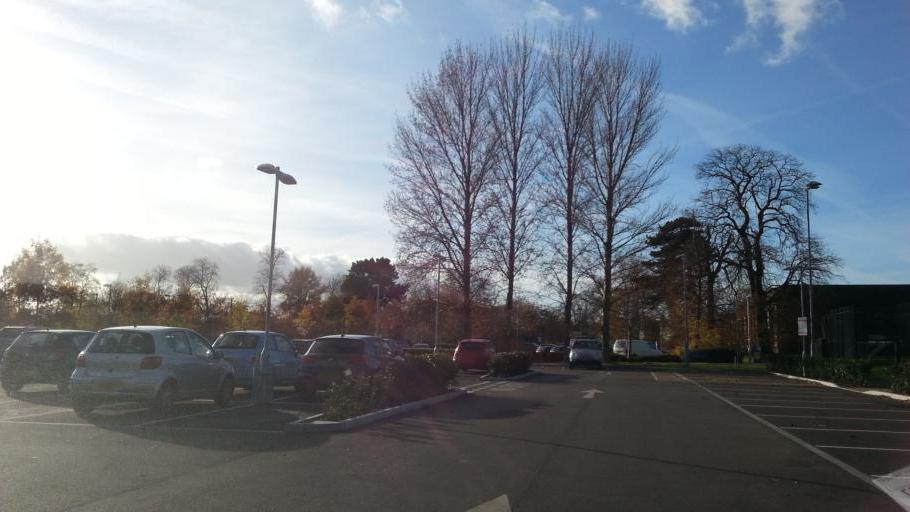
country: GB
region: England
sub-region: Reading
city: Reading
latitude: 51.4426
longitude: -0.9507
